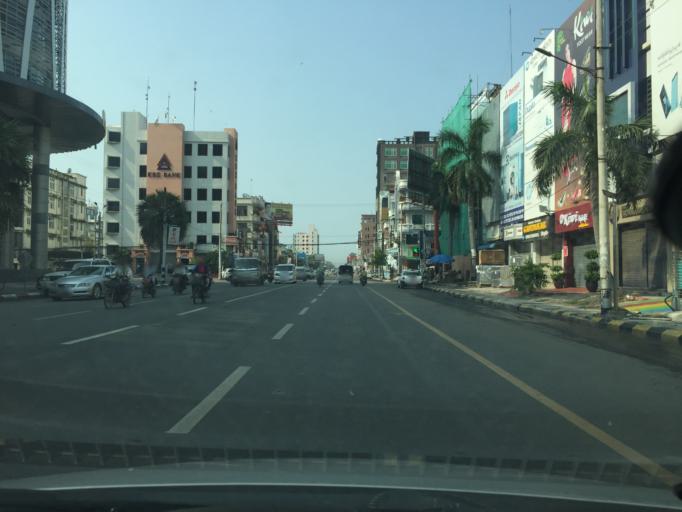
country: MM
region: Mandalay
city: Mandalay
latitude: 21.9714
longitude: 96.0865
